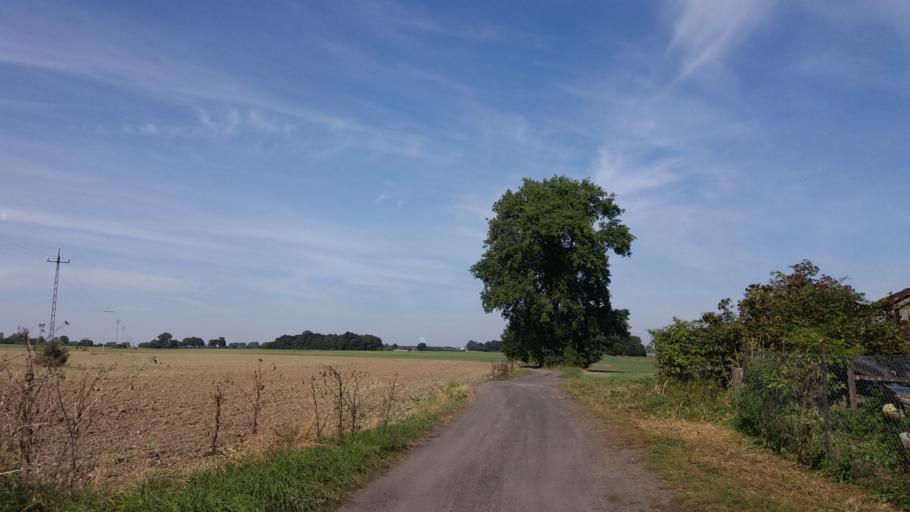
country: PL
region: West Pomeranian Voivodeship
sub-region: Powiat choszczenski
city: Choszczno
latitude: 53.1295
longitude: 15.4061
